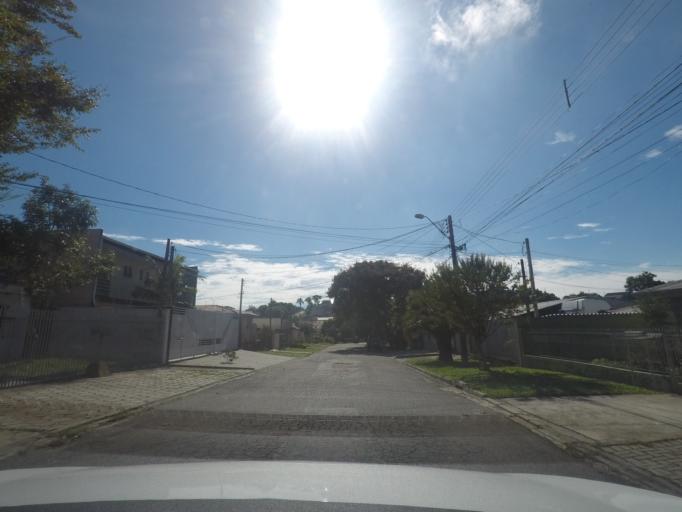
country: BR
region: Parana
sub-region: Sao Jose Dos Pinhais
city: Sao Jose dos Pinhais
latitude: -25.5091
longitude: -49.2775
